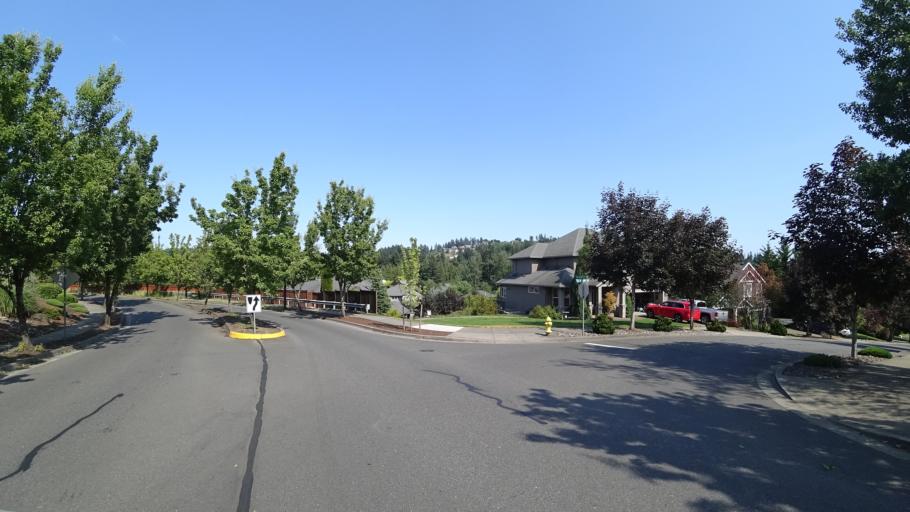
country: US
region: Oregon
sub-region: Clackamas County
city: Happy Valley
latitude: 45.4419
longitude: -122.5378
